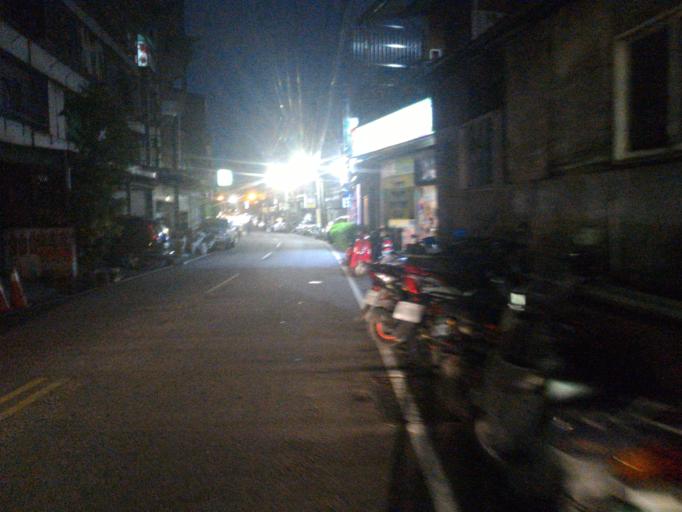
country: TW
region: Taipei
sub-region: Taipei
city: Banqiao
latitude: 24.9771
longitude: 121.4186
